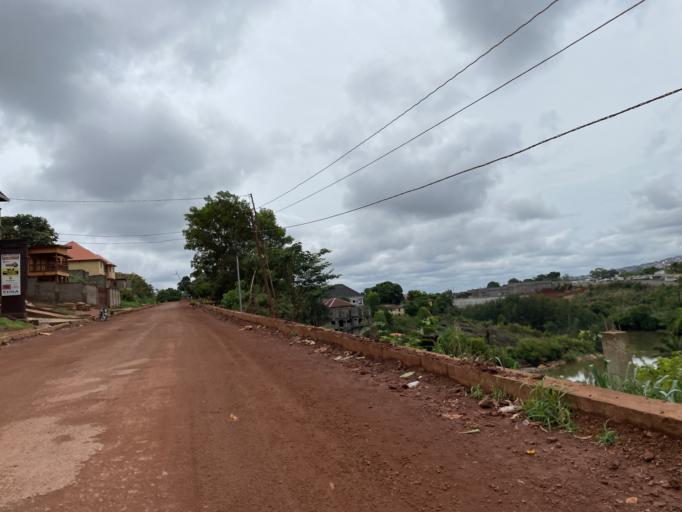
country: SL
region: Western Area
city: Hastings
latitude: 8.3987
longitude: -13.1486
